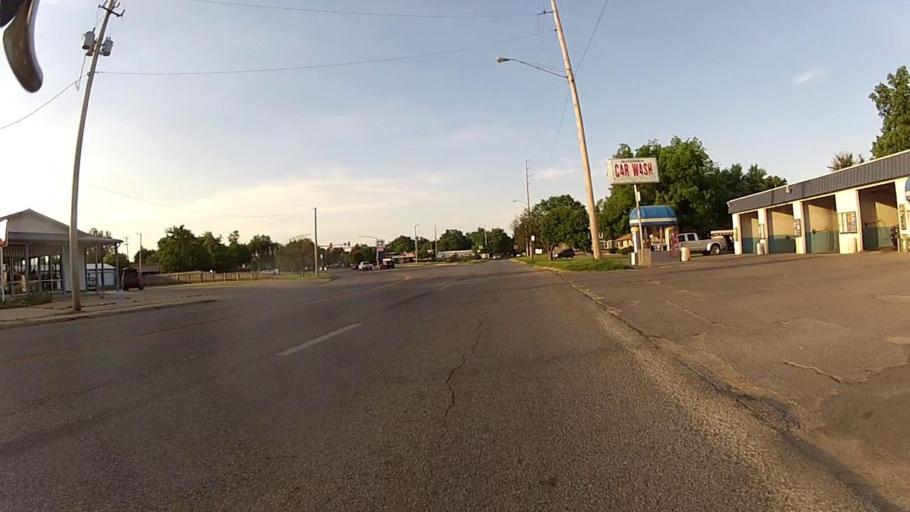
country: US
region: Kansas
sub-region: Cowley County
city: Arkansas City
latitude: 37.0790
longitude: -97.0401
